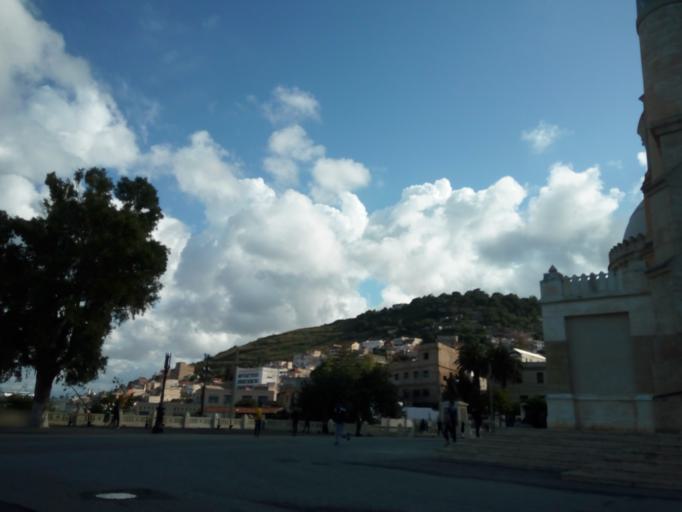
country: DZ
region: Alger
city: Algiers
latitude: 36.8013
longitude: 3.0430
